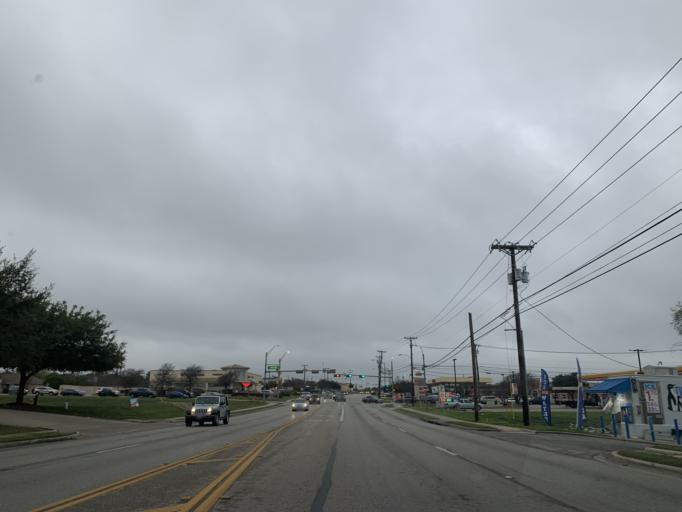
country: US
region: Texas
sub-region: Travis County
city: Windemere
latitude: 30.4972
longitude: -97.6121
